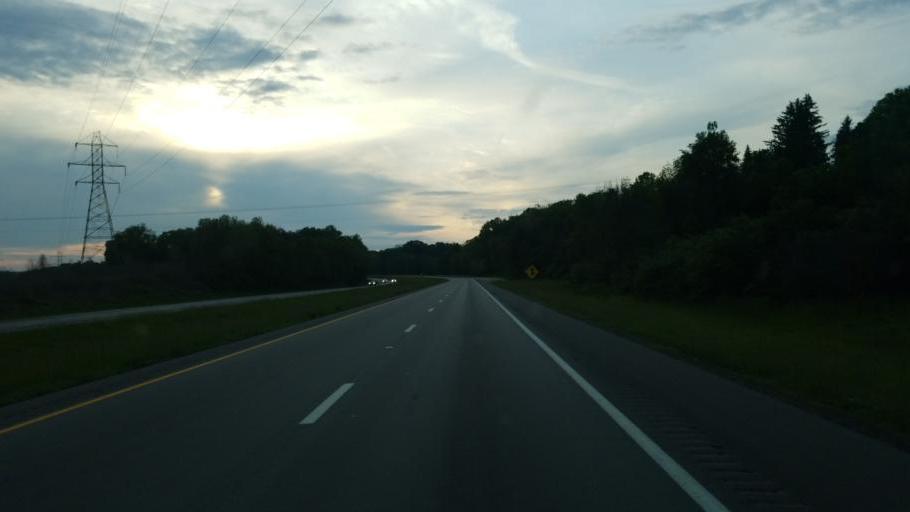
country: US
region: Ohio
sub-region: Stark County
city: Brewster
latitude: 40.7693
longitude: -81.5827
